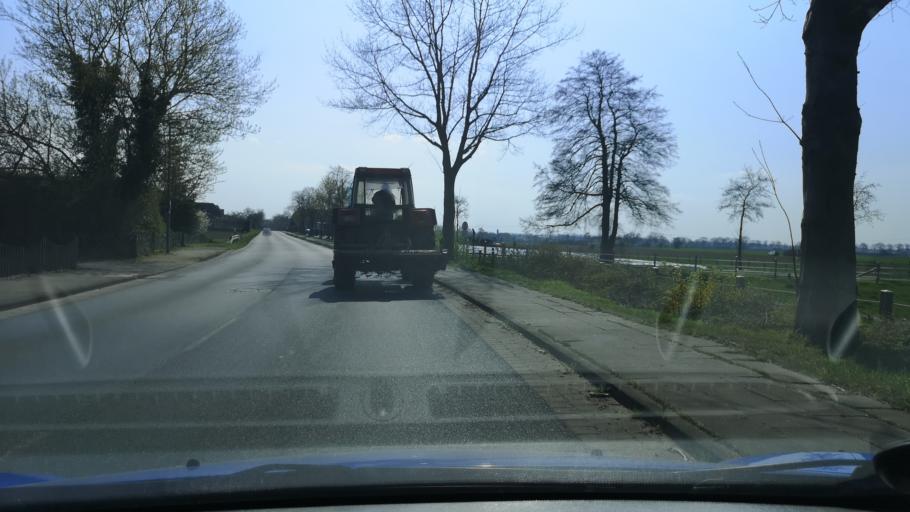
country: DE
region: Lower Saxony
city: Neustadt am Rubenberge
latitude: 52.5282
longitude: 9.4802
